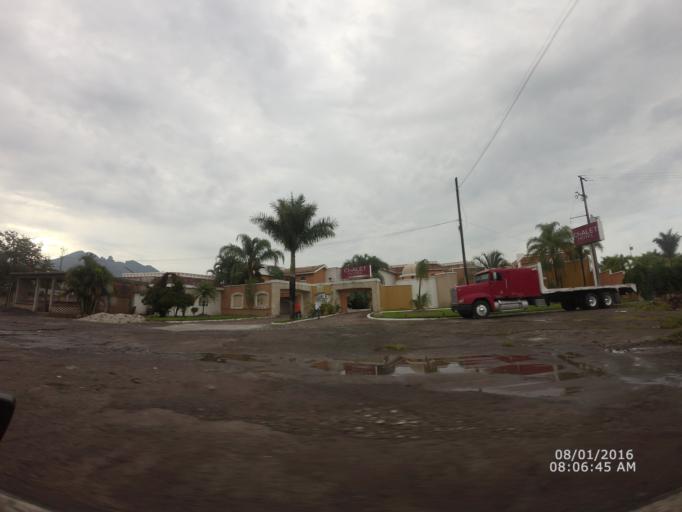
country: MX
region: Nayarit
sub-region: Tepic
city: La Corregidora
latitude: 21.4483
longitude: -104.8159
